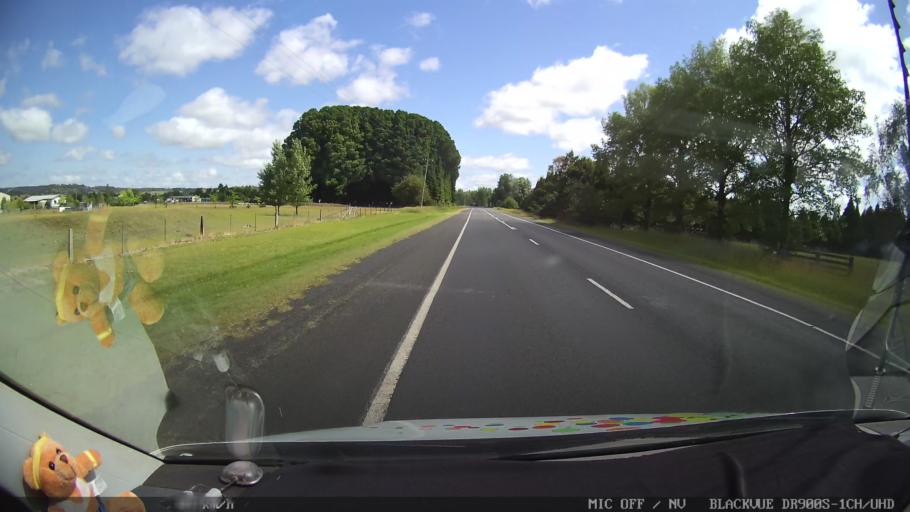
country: AU
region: New South Wales
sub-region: Glen Innes Severn
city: Glen Innes
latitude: -29.8158
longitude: 151.7410
